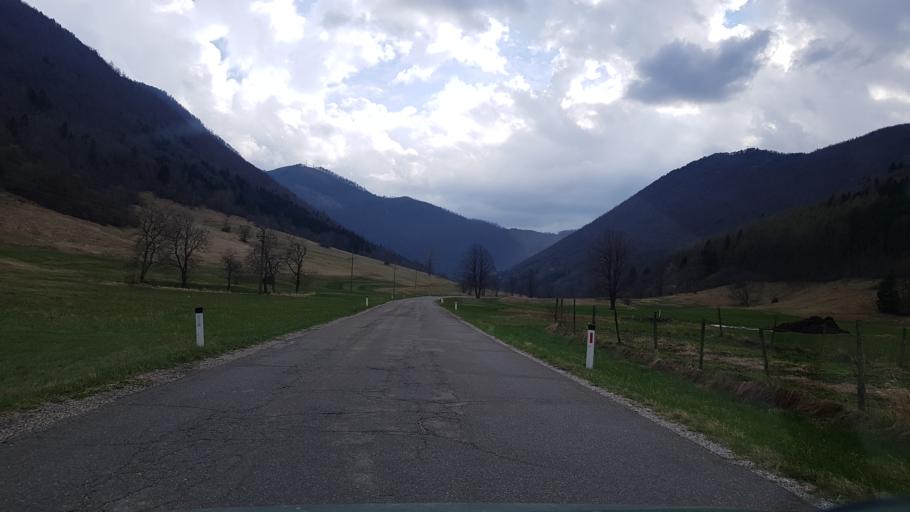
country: SI
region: Nova Gorica
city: Sempas
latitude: 46.0445
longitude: 13.7902
